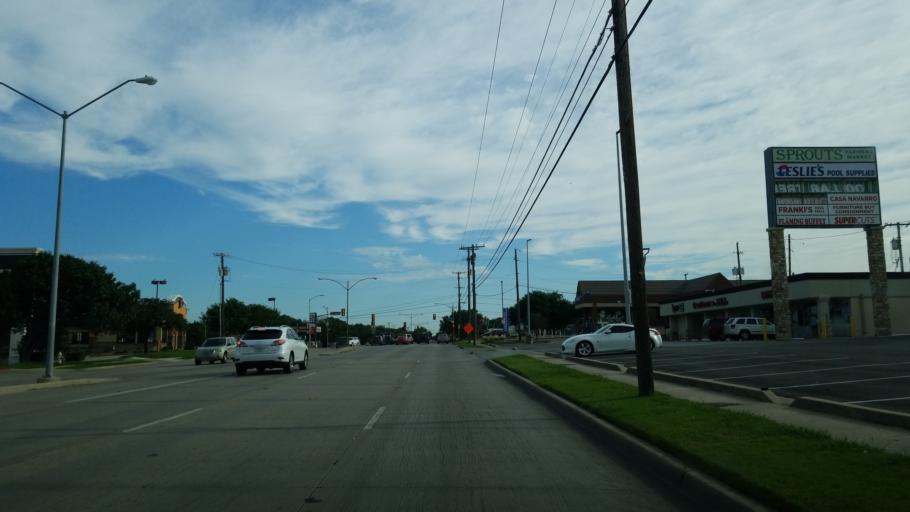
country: US
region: Texas
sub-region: Dallas County
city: Farmers Branch
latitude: 32.9082
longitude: -96.8560
